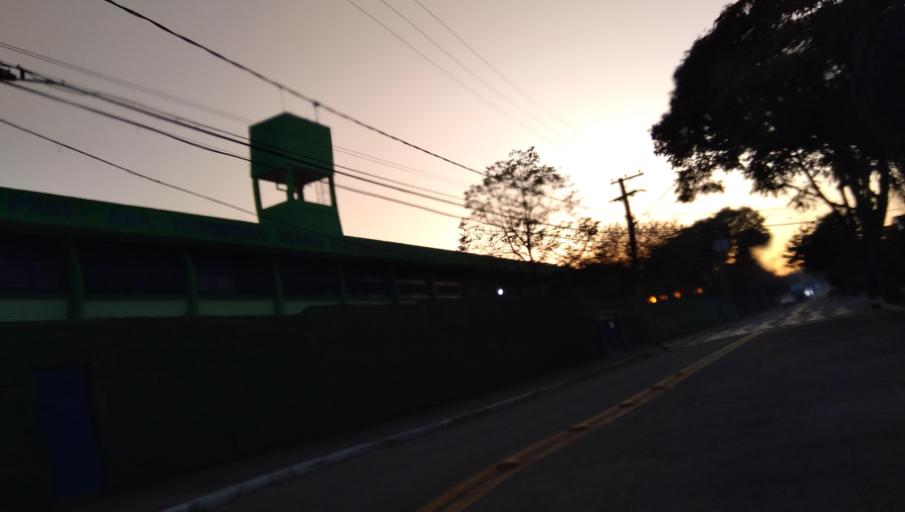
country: BR
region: Sao Paulo
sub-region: Sao Jose Dos Campos
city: Sao Jose dos Campos
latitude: -23.1770
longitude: -45.8208
